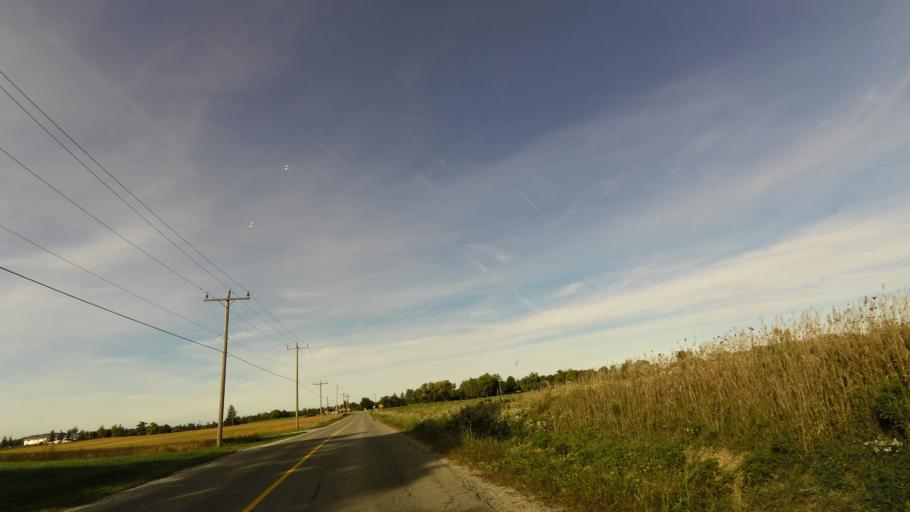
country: CA
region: Ontario
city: Ancaster
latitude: 43.1194
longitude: -79.9581
